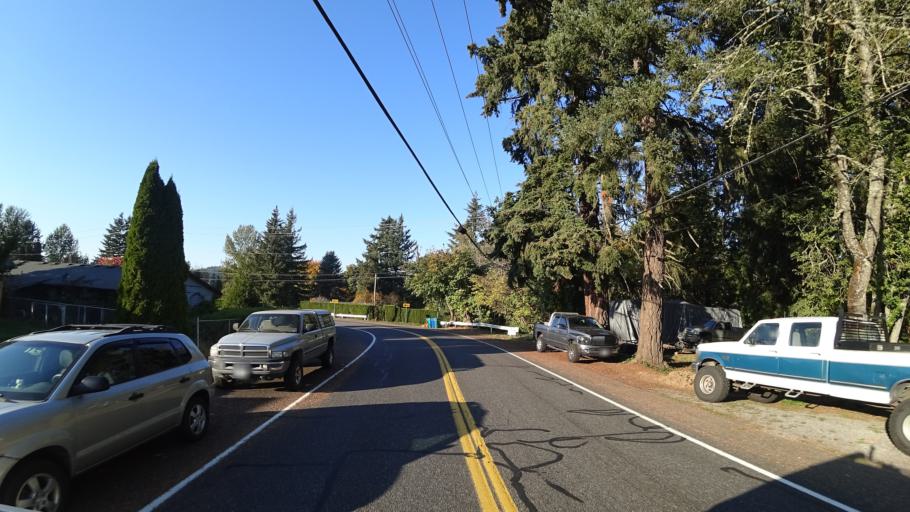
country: US
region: Oregon
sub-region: Multnomah County
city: Gresham
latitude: 45.4864
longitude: -122.4536
